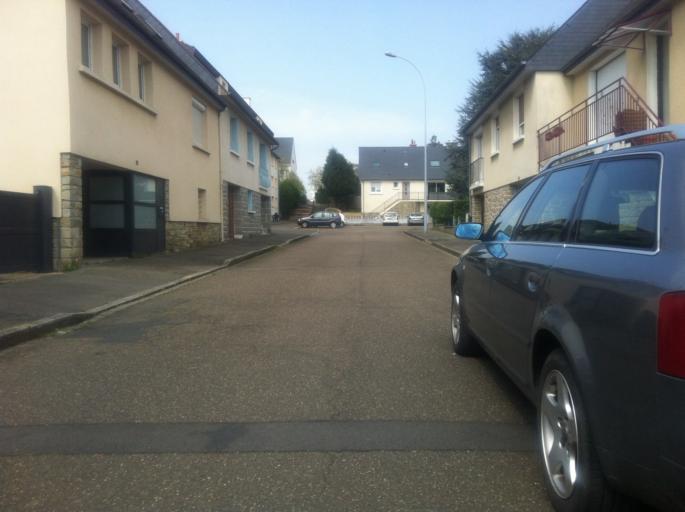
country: FR
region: Brittany
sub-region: Departement d'Ille-et-Vilaine
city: Bruz
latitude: 48.0238
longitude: -1.7427
